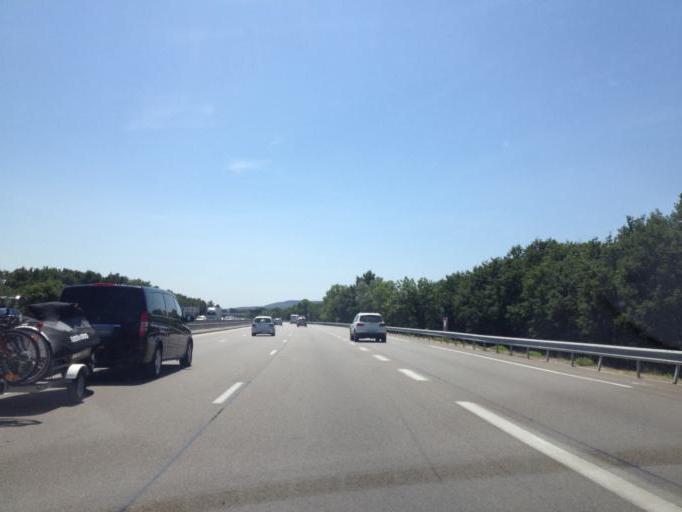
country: FR
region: Rhone-Alpes
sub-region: Departement de la Drome
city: Allan
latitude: 44.5113
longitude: 4.7761
